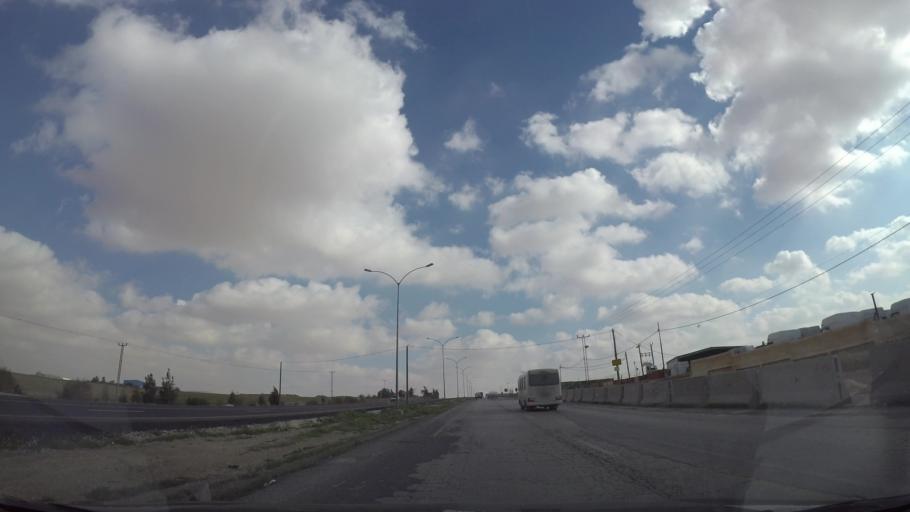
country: JO
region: Amman
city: Al Jizah
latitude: 31.6856
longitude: 35.9613
